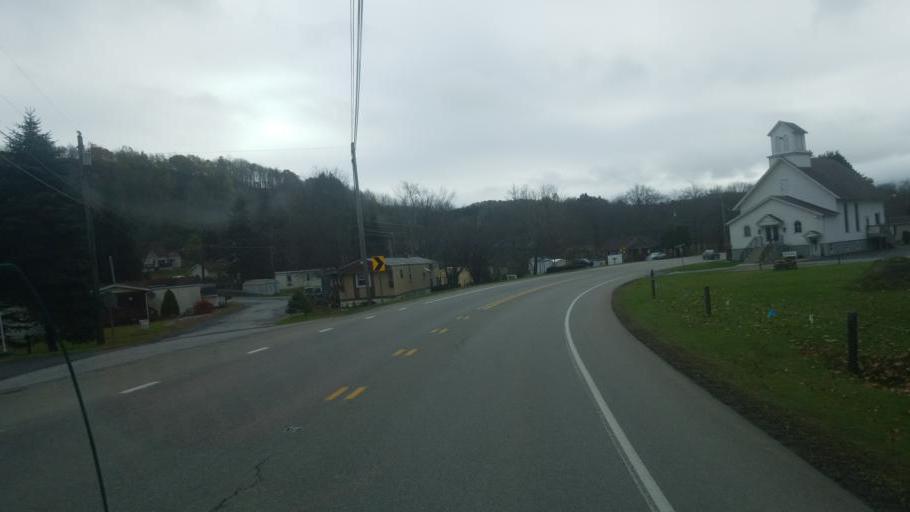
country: US
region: Pennsylvania
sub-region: Jefferson County
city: Brockway
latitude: 41.2641
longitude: -78.7213
